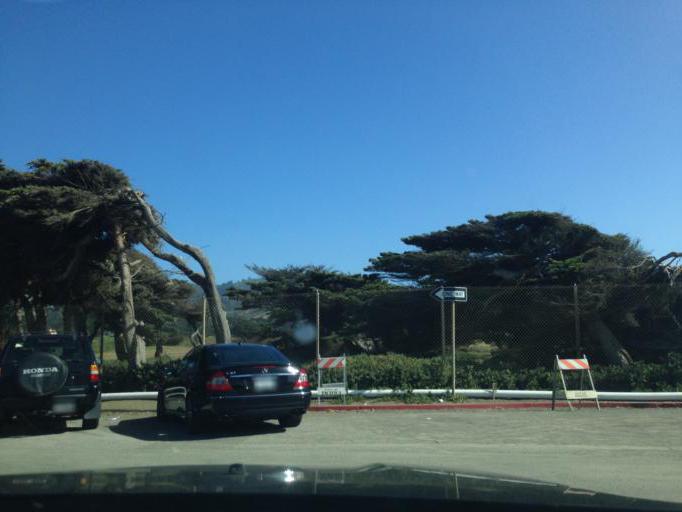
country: US
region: California
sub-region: San Mateo County
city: Pacifica
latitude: 37.6300
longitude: -122.4939
